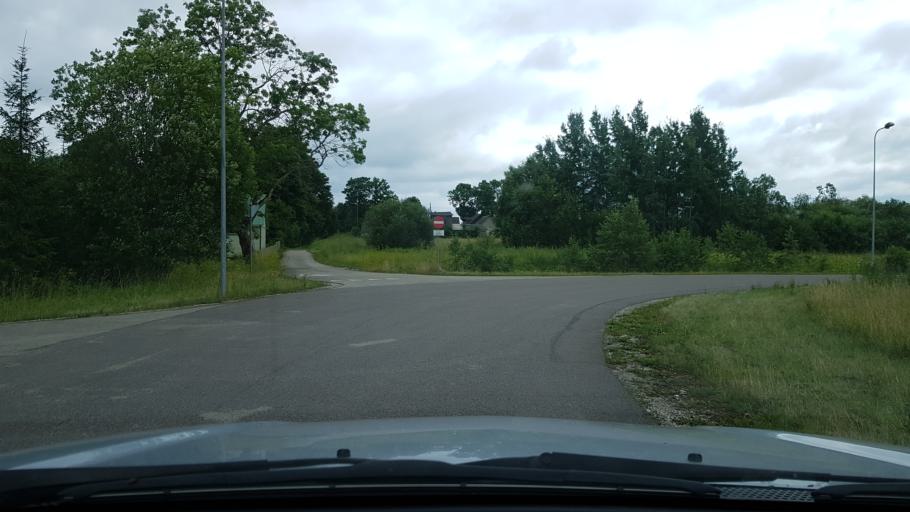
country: EE
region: Ida-Virumaa
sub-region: Narva linn
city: Narva
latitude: 59.3958
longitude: 28.1215
